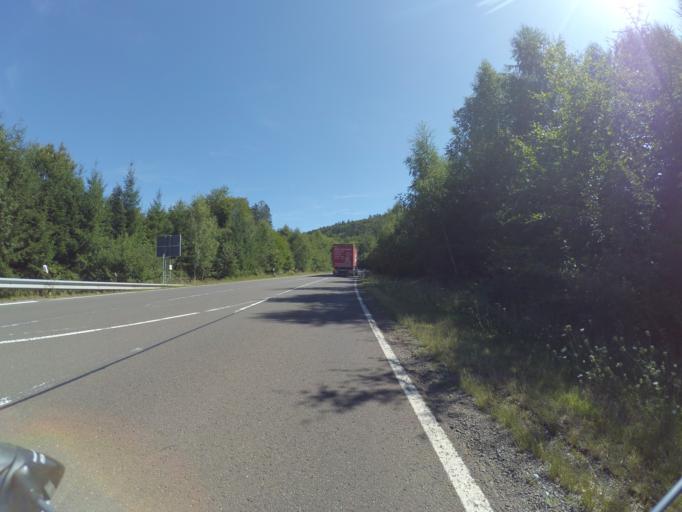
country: DE
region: Rheinland-Pfalz
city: Deuselbach
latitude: 49.7457
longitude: 7.0577
